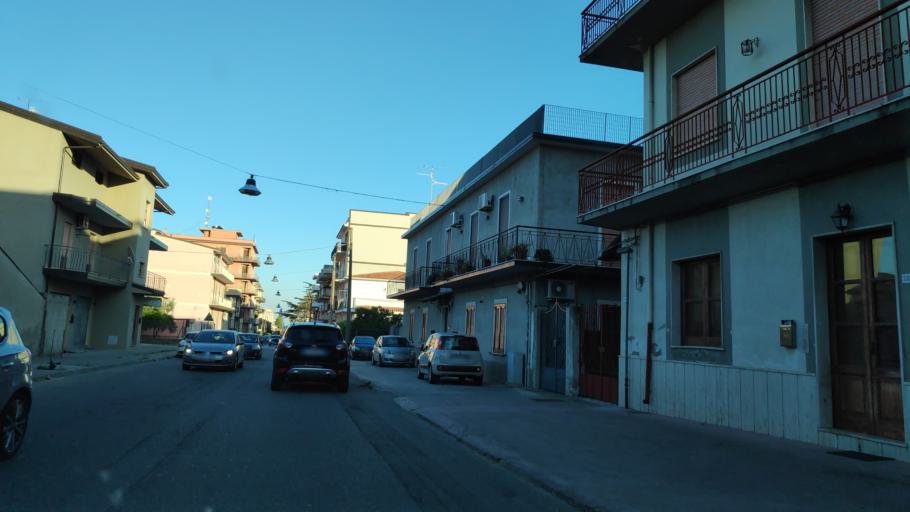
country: IT
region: Calabria
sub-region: Provincia di Reggio Calabria
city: Locri
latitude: 38.2391
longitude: 16.2549
